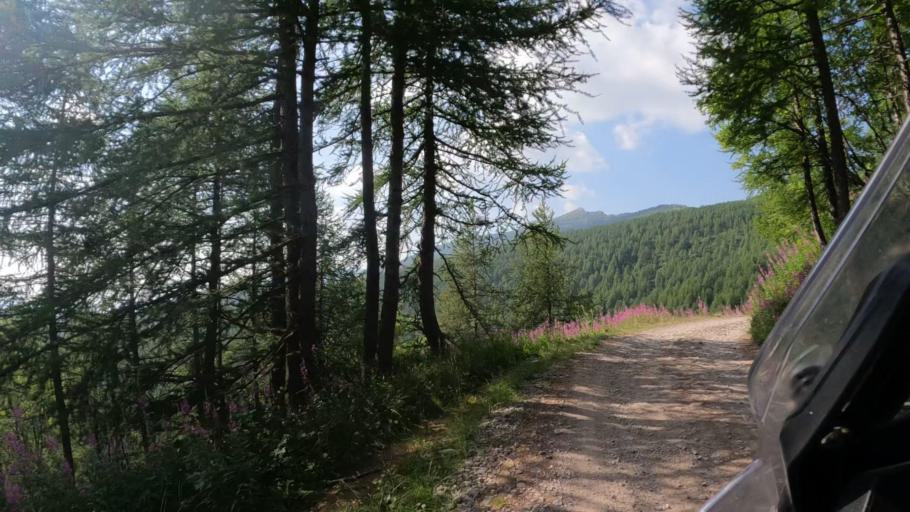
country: IT
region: Piedmont
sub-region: Provincia di Cuneo
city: Briga Alta
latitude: 44.1255
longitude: 7.6922
